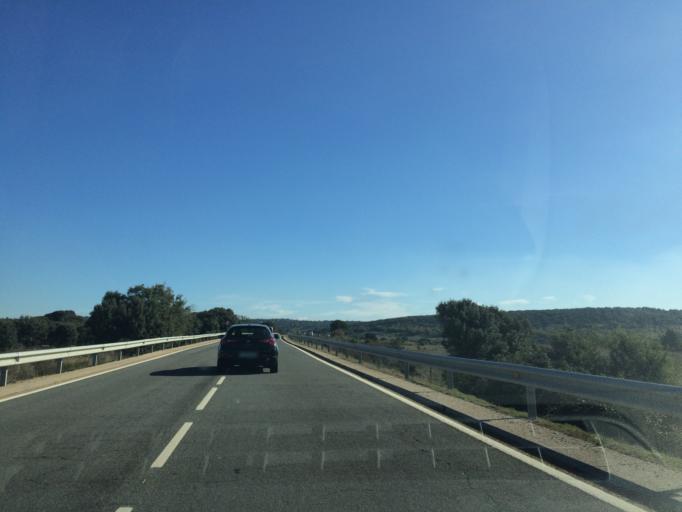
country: ES
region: Madrid
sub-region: Provincia de Madrid
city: Venturada
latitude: 40.7806
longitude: -3.6487
